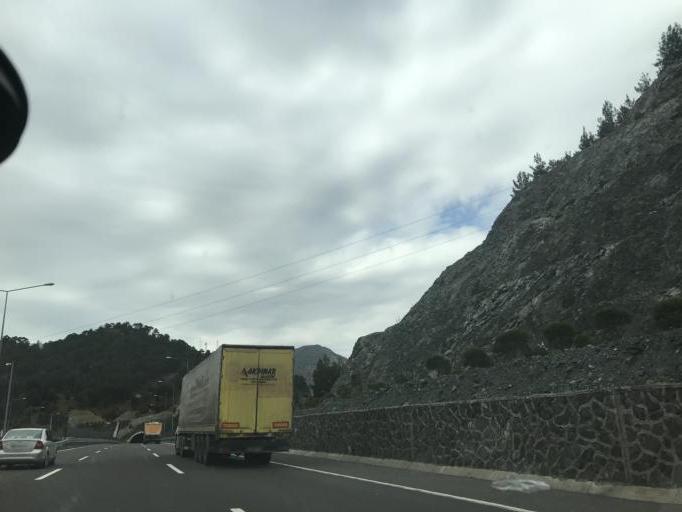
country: TR
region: Nigde
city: Ciftehan
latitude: 37.5051
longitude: 34.8215
